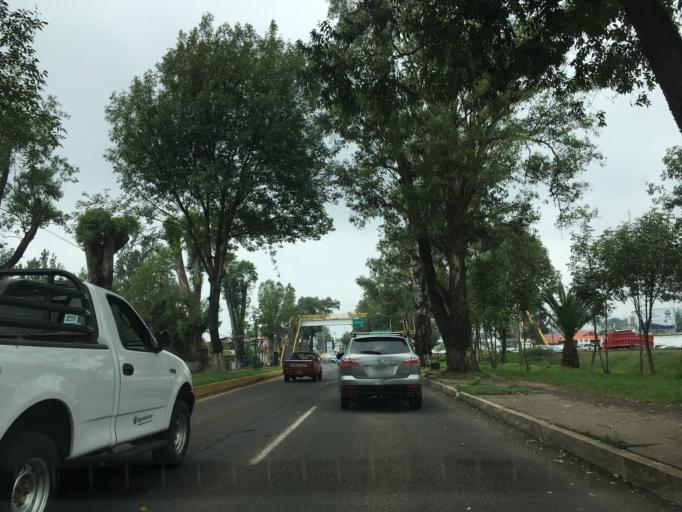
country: MX
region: Michoacan
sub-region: Uruapan
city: Toreo Bajo (El Toreo Bajo)
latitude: 19.4242
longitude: -102.0170
